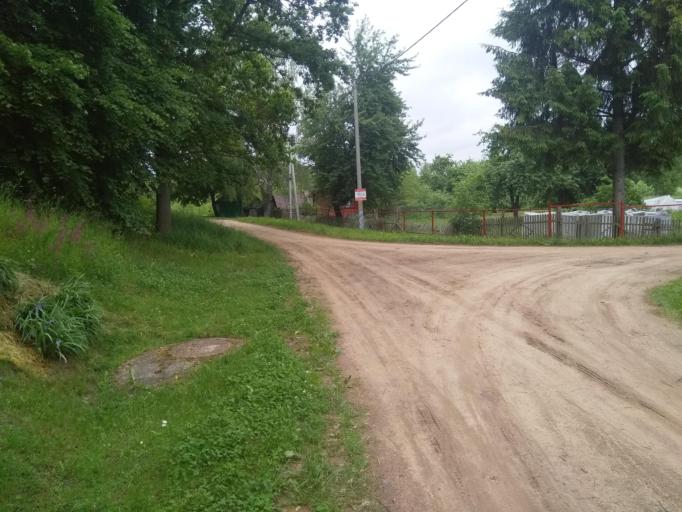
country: BY
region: Mogilev
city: Mahilyow
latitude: 53.9102
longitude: 30.4093
